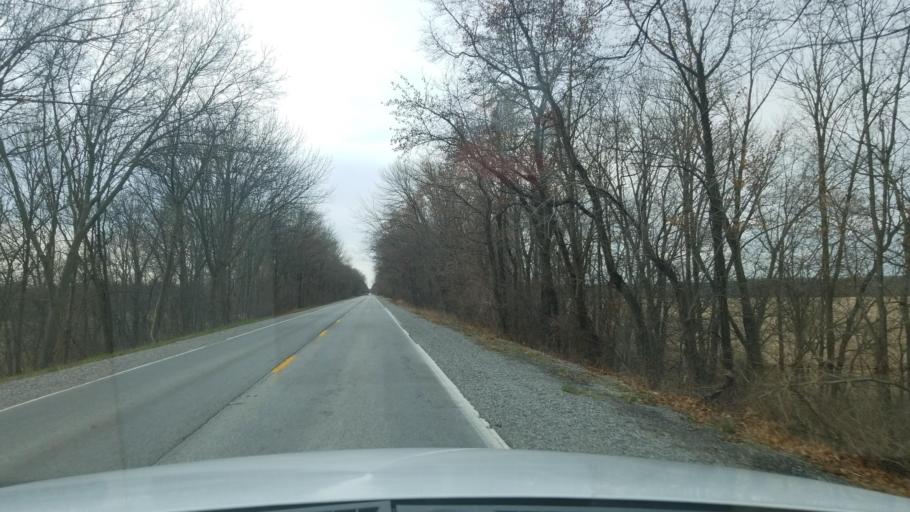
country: US
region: Illinois
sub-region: White County
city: Carmi
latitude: 37.9268
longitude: -88.0990
